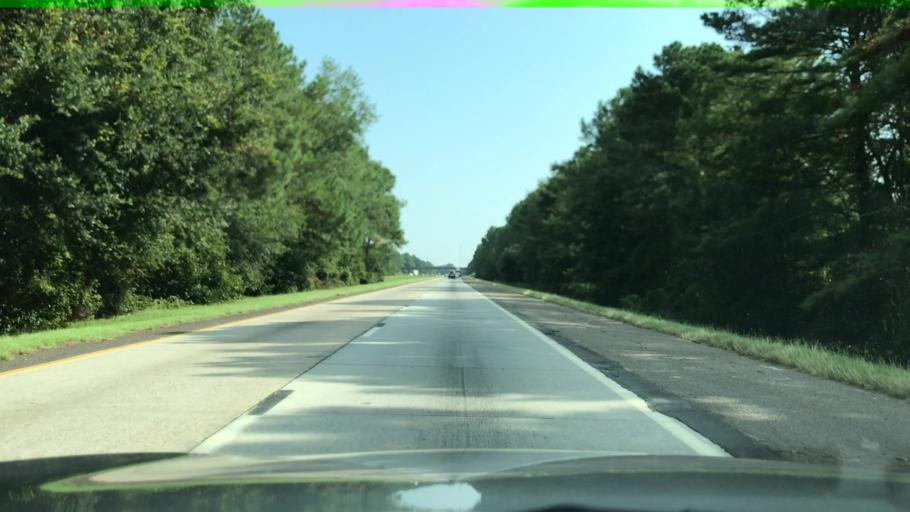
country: US
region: South Carolina
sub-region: Hampton County
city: Yemassee
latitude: 32.7778
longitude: -80.7942
